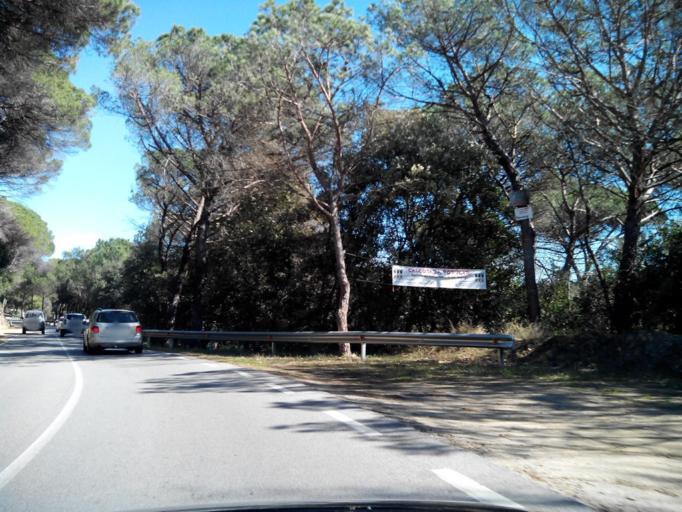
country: ES
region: Catalonia
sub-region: Provincia de Barcelona
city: Dosrius
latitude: 41.5932
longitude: 2.4320
